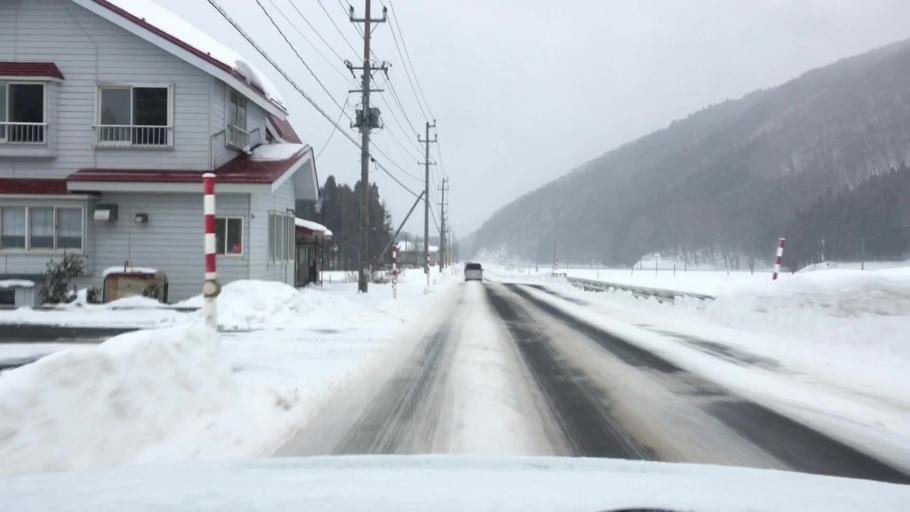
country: JP
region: Akita
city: Hanawa
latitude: 40.0357
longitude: 140.9915
